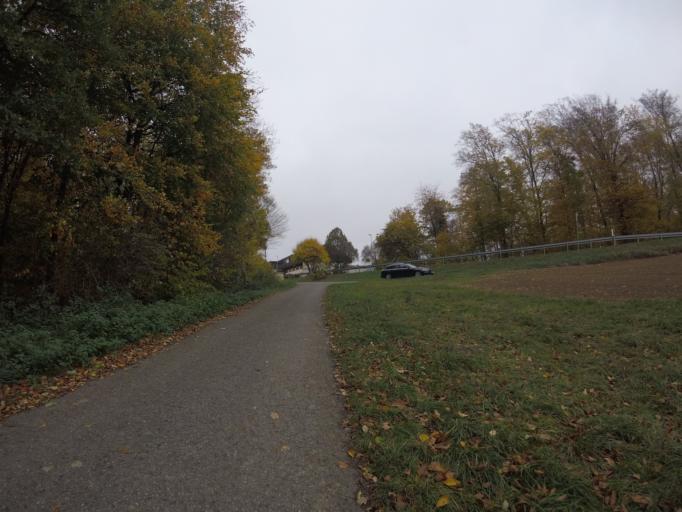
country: DE
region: Baden-Wuerttemberg
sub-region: Regierungsbezirk Stuttgart
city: Grossbottwar
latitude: 48.9790
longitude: 9.3109
